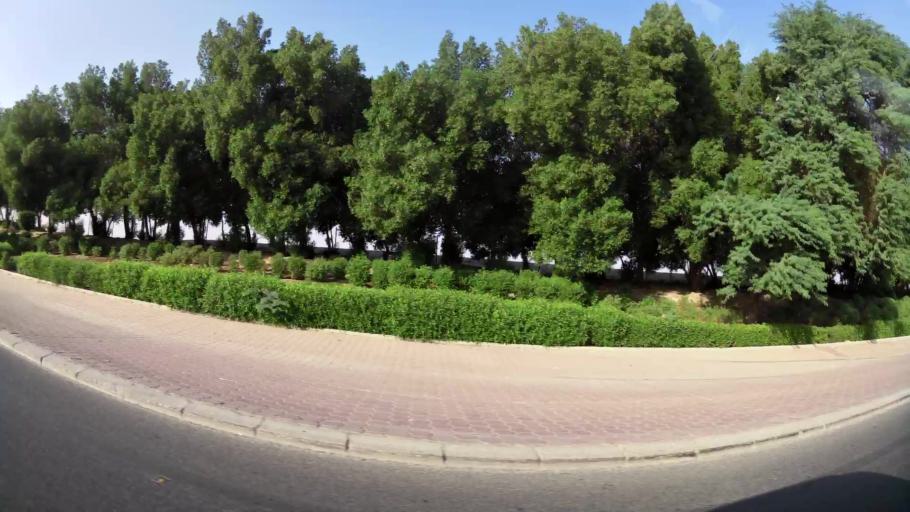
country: KW
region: Al Farwaniyah
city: Janub as Surrah
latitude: 29.2609
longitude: 47.9882
